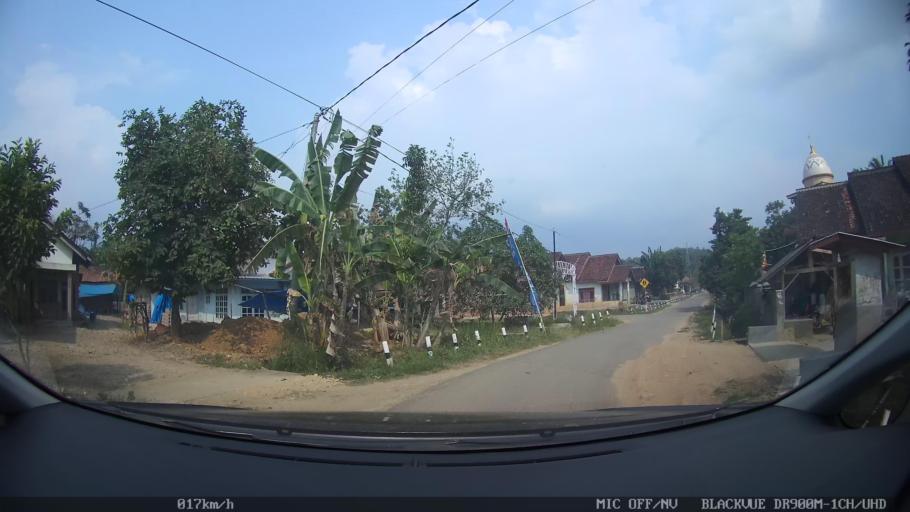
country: ID
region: Lampung
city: Kedondong
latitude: -5.4090
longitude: 105.0085
